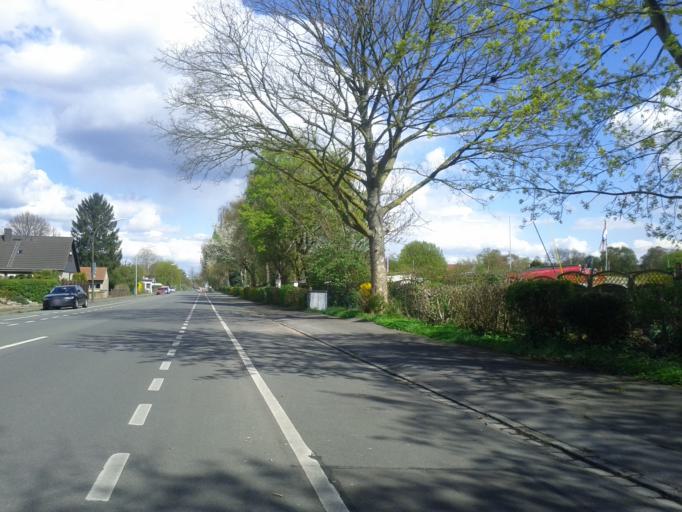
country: DE
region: North Rhine-Westphalia
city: Lanstrop
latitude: 51.5759
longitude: 7.5587
